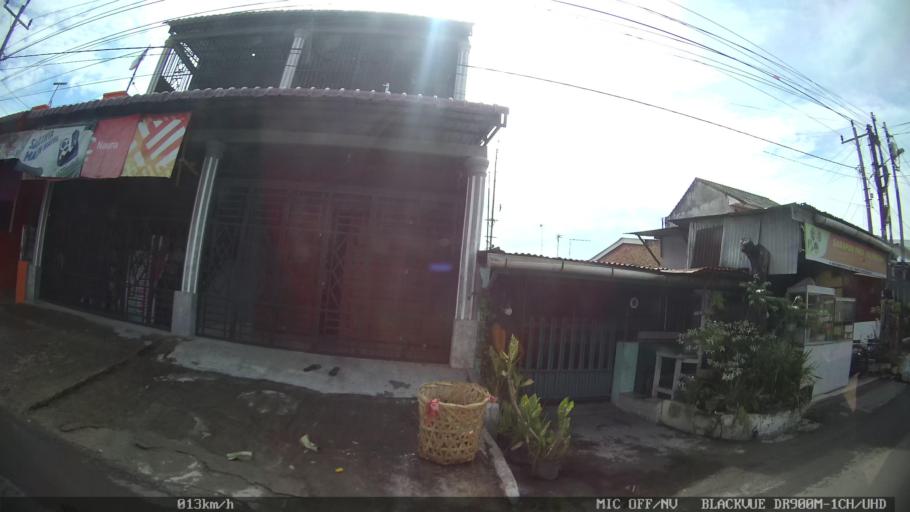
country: ID
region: North Sumatra
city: Medan
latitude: 3.6113
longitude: 98.6403
